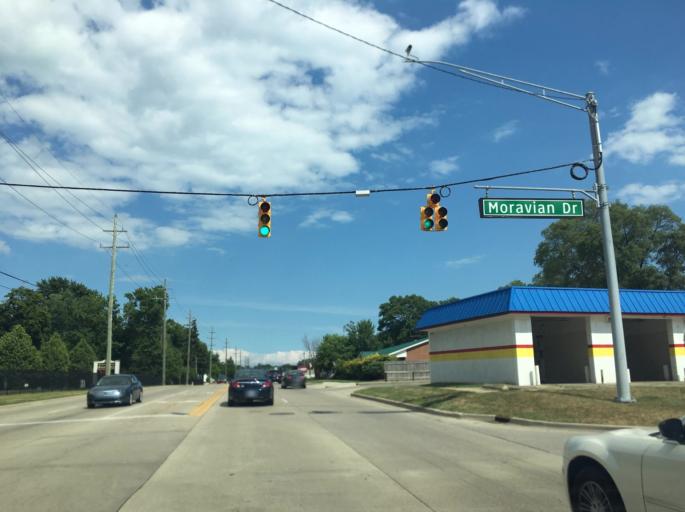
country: US
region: Michigan
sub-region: Macomb County
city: Clinton
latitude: 42.6003
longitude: -82.9056
